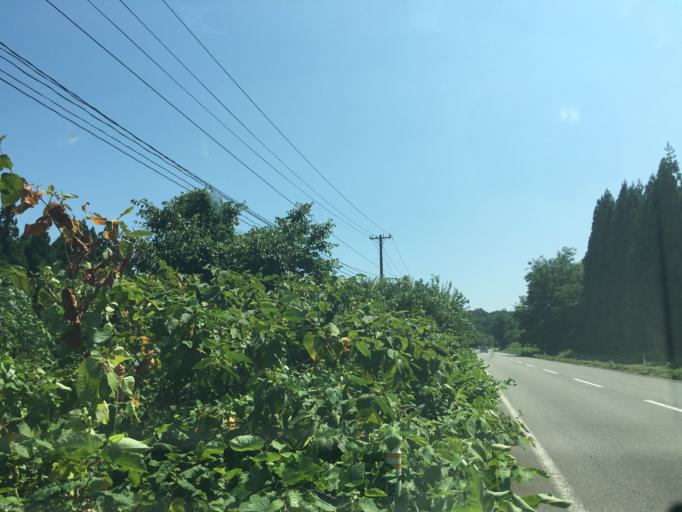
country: JP
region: Akita
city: Tenno
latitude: 39.9779
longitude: 139.7372
